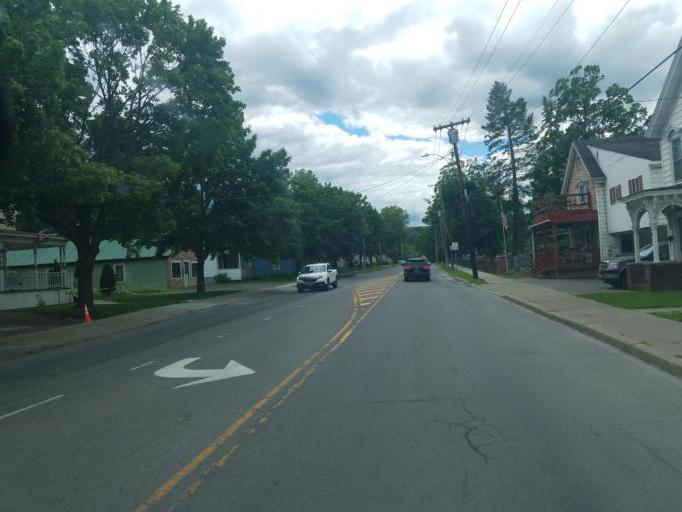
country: US
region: New York
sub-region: Herkimer County
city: Mohawk
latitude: 43.0077
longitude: -75.0057
